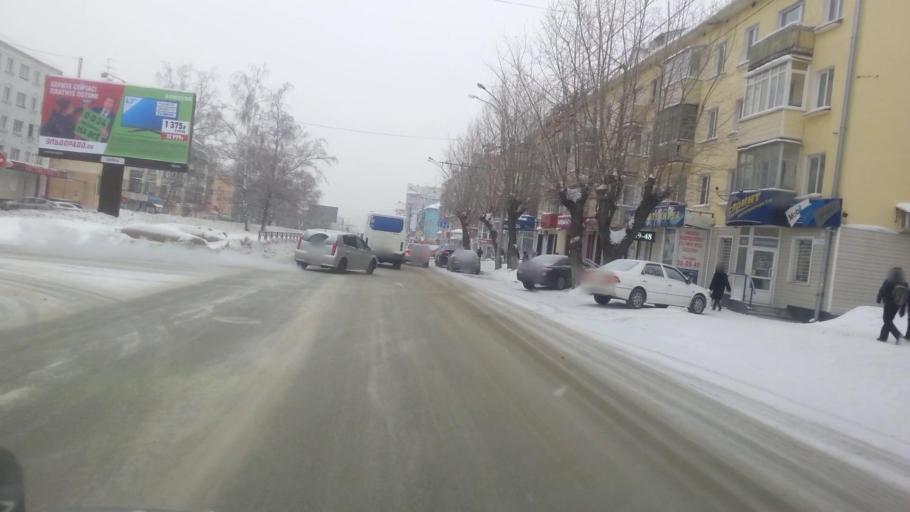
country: RU
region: Altai Krai
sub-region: Gorod Barnaulskiy
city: Barnaul
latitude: 53.3745
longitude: 83.7477
